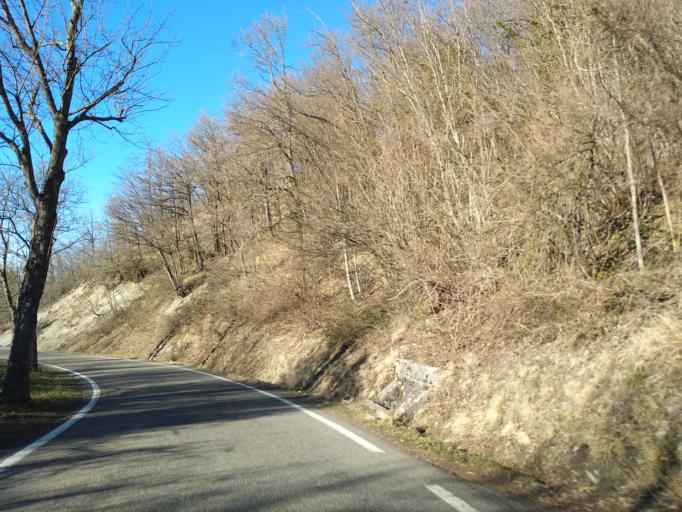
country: IT
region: Emilia-Romagna
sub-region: Provincia di Reggio Emilia
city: Castelnovo ne'Monti
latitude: 44.4204
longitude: 10.4069
